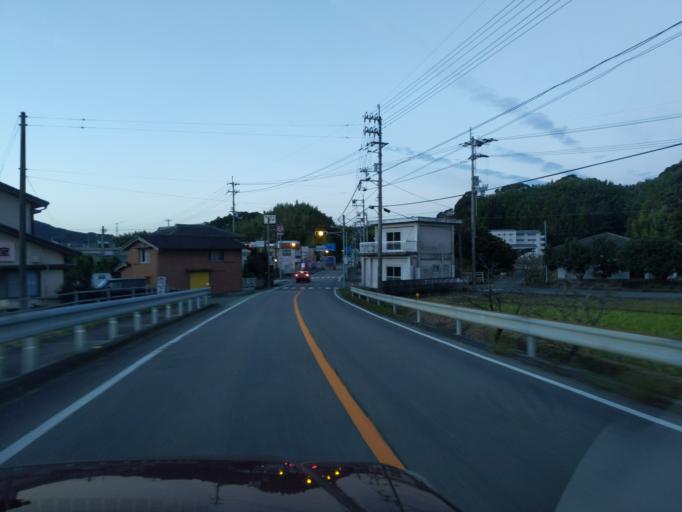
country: JP
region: Tokushima
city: Anan
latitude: 33.8429
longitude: 134.6242
